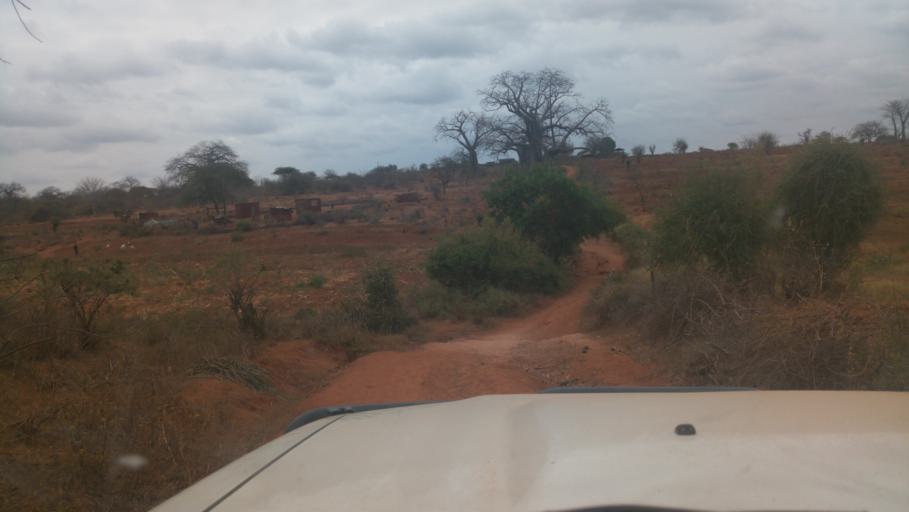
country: KE
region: Makueni
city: Makueni
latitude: -1.9674
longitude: 38.0790
